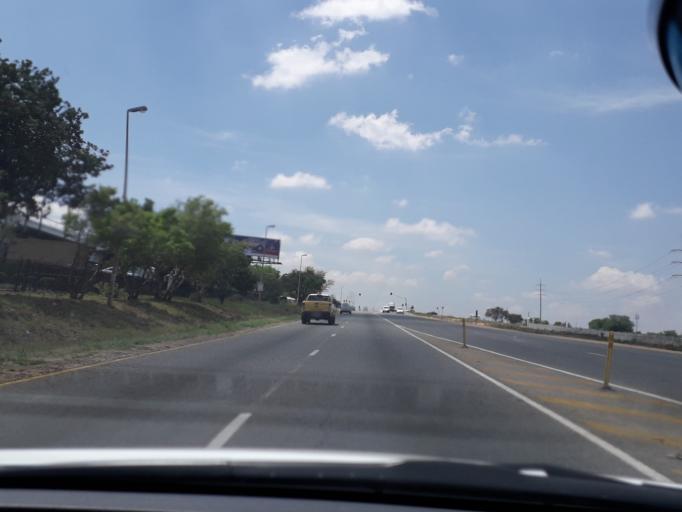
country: ZA
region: Gauteng
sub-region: City of Johannesburg Metropolitan Municipality
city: Midrand
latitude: -26.0120
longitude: 28.1304
